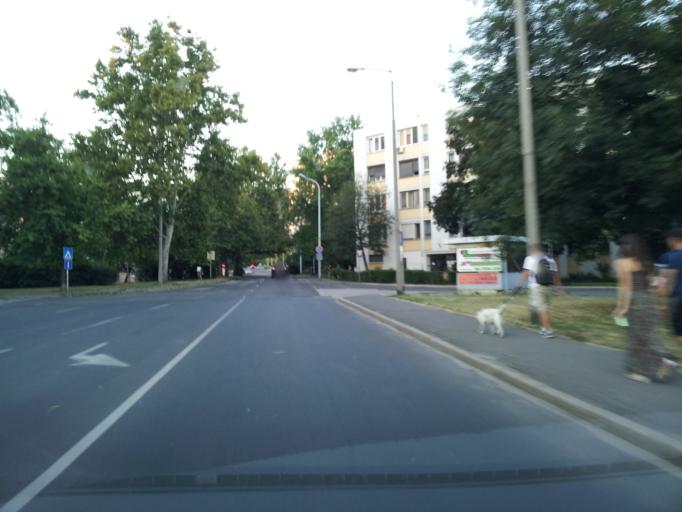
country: HU
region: Komarom-Esztergom
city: Tatabanya
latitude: 47.5762
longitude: 18.4045
